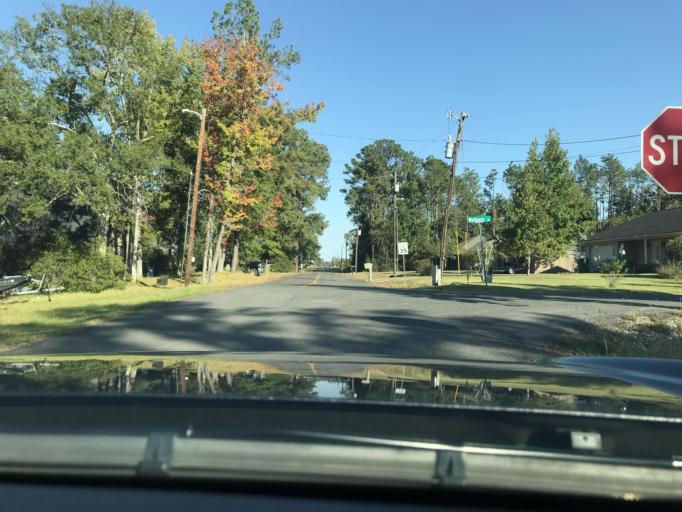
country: US
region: Louisiana
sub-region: Calcasieu Parish
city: Westlake
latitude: 30.3153
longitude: -93.2743
